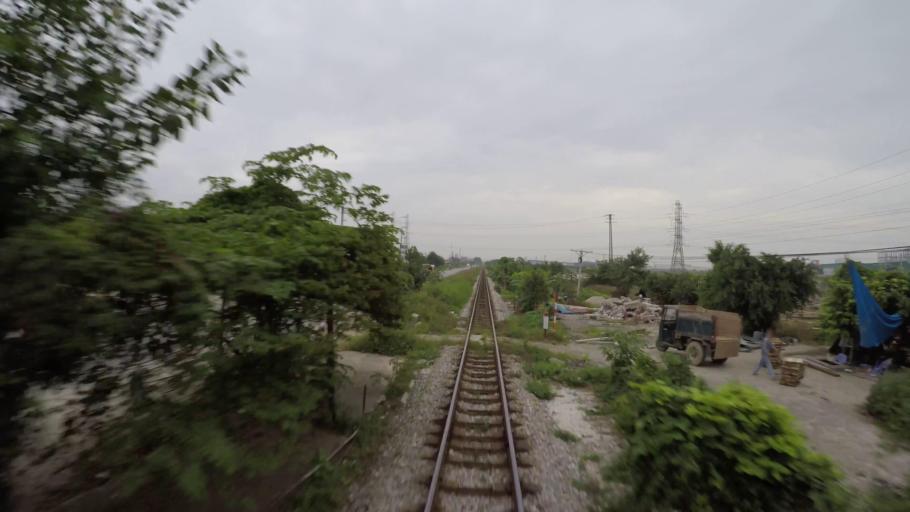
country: VN
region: Hung Yen
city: Ban Yen Nhan
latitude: 20.9855
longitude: 106.0402
